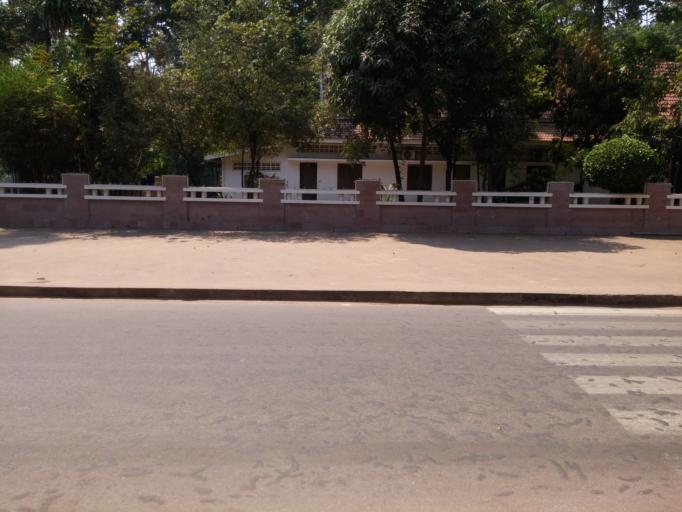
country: KH
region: Siem Reap
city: Siem Reap
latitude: 13.3612
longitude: 103.8597
